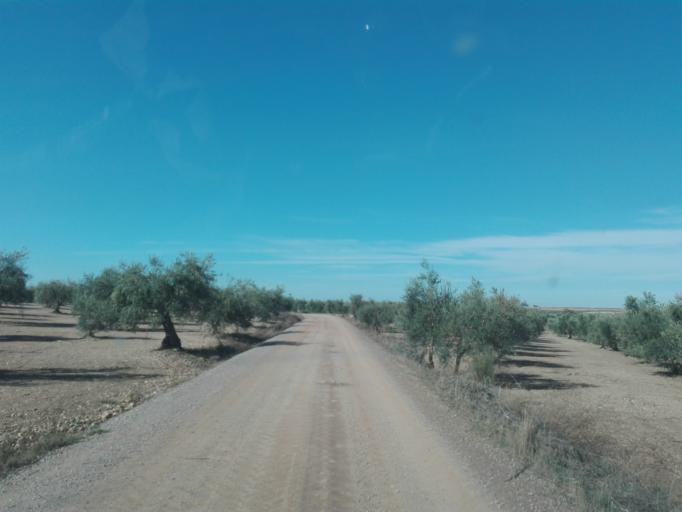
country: ES
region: Extremadura
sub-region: Provincia de Badajoz
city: Ahillones
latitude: 38.2827
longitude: -5.9047
